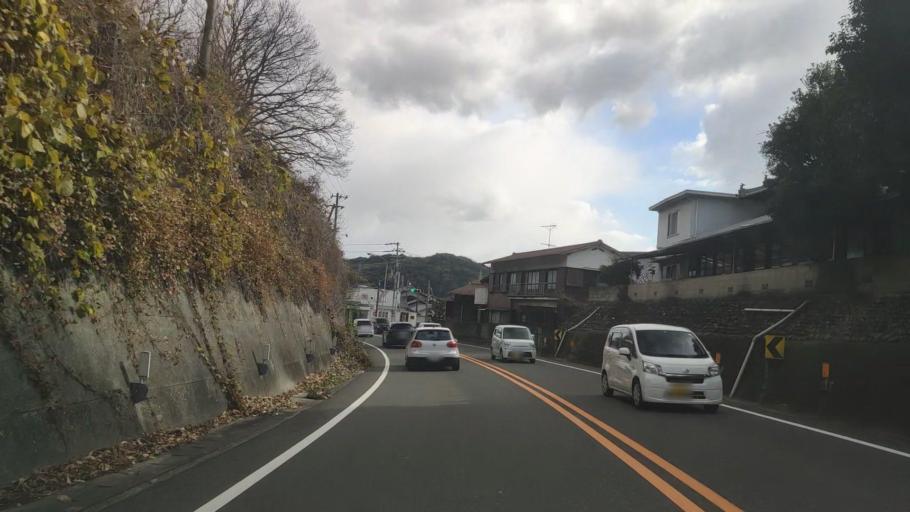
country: JP
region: Ehime
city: Hojo
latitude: 34.0601
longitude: 132.9170
